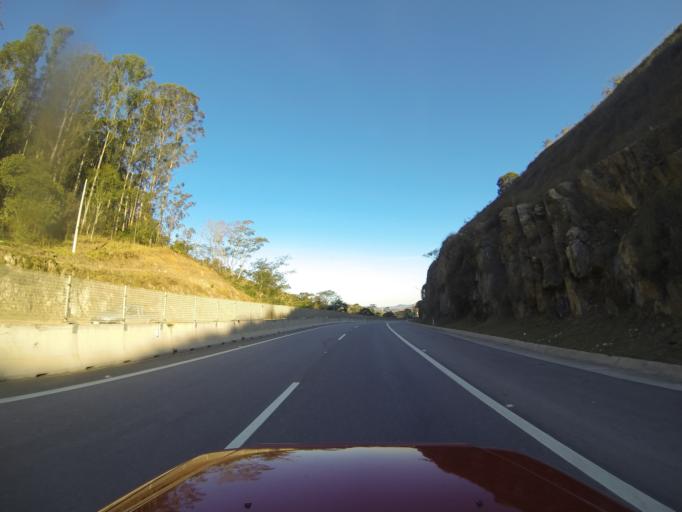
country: BR
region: Sao Paulo
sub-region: Santa Branca
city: Santa Branca
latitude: -23.2961
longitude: -45.7791
